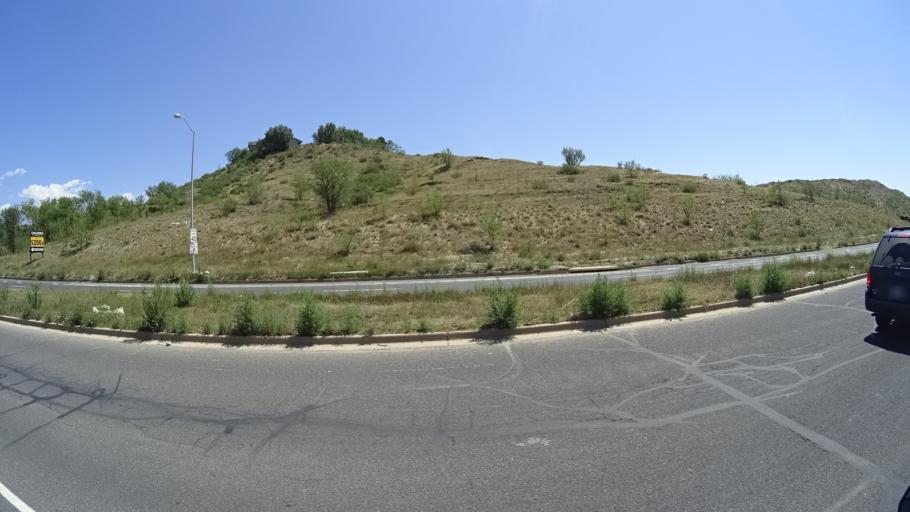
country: US
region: Colorado
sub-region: El Paso County
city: Stratmoor
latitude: 38.8015
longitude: -104.7858
